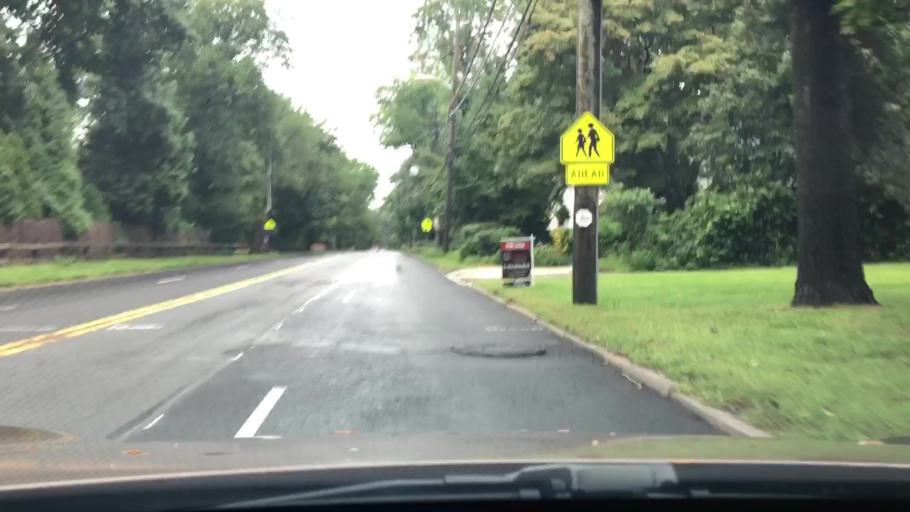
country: US
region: New York
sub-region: Westchester County
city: Greenville
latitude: 40.9834
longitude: -73.7989
